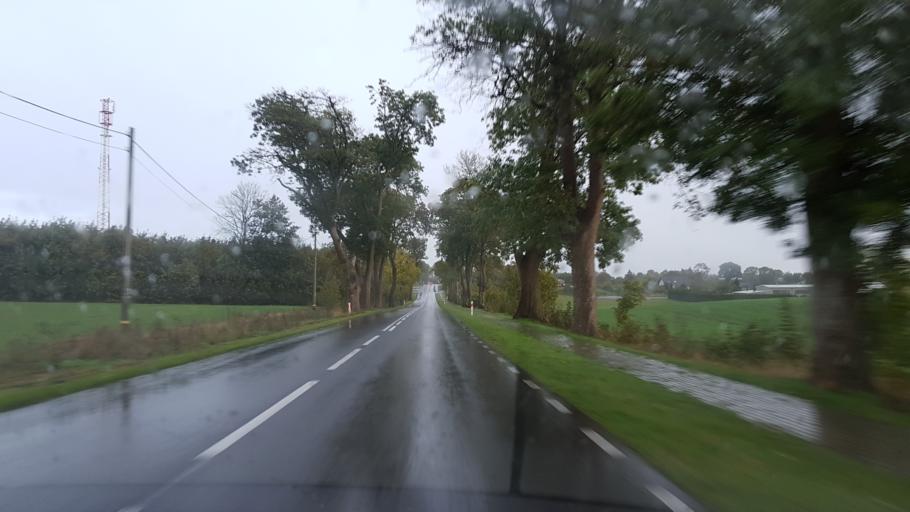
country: PL
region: Greater Poland Voivodeship
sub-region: Powiat pilski
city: Szydlowo
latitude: 53.1697
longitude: 16.5858
